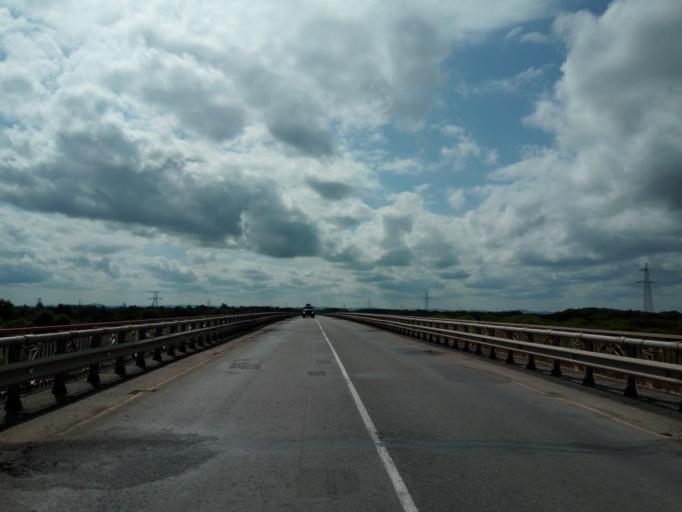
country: RU
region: Primorskiy
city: Dal'nerechensk
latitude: 45.9610
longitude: 133.7837
